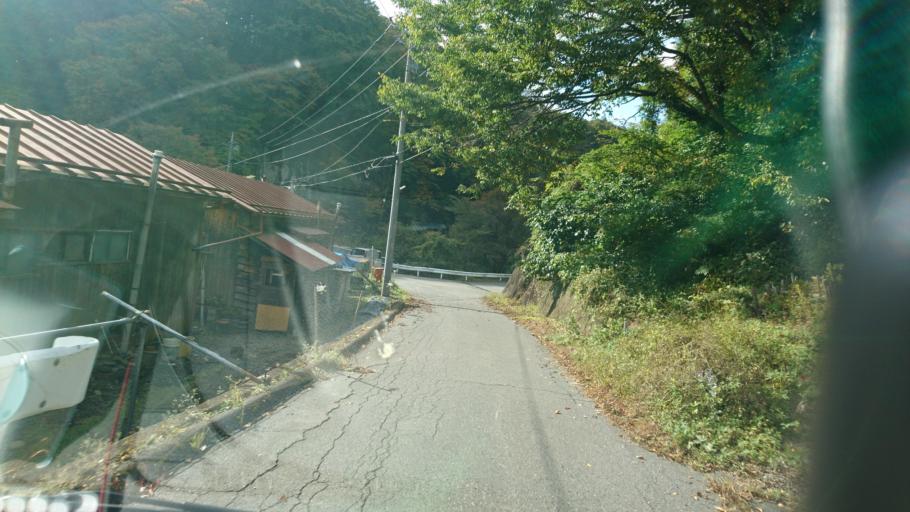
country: JP
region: Gunma
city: Omamacho-omama
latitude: 36.6062
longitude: 139.2374
